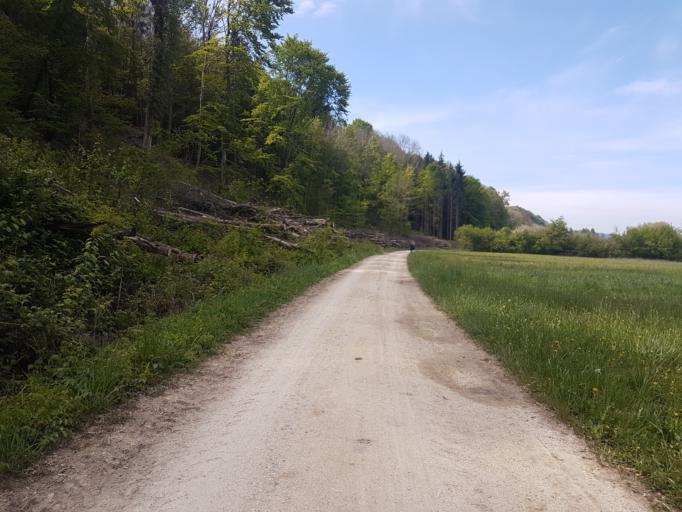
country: CH
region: Bern
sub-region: Seeland District
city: Tauffelen
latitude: 47.0667
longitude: 7.1893
